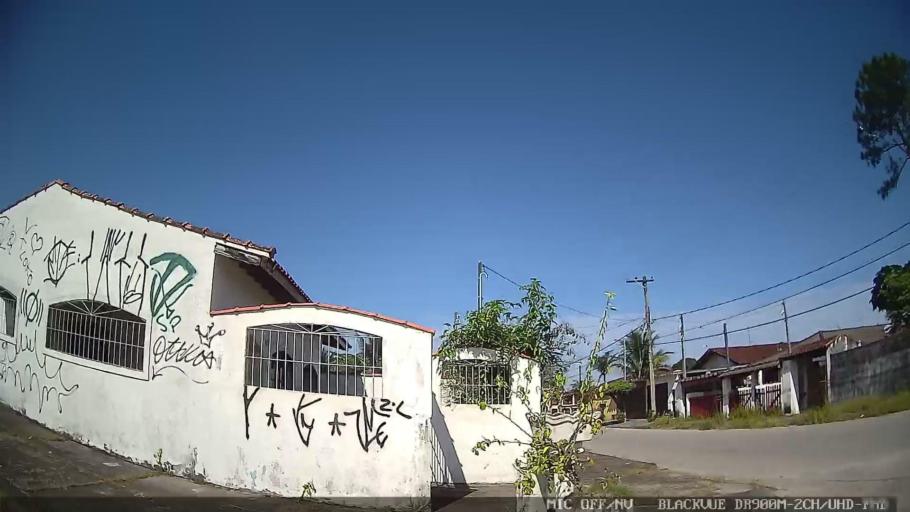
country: BR
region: Sao Paulo
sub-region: Itanhaem
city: Itanhaem
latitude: -24.1491
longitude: -46.7363
